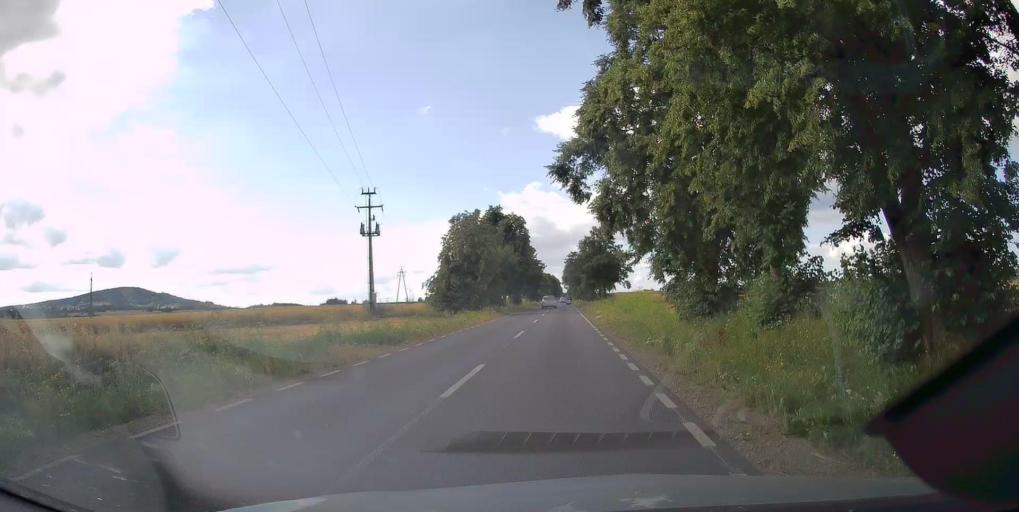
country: PL
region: Swietokrzyskie
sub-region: Powiat kielecki
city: Bodzentyn
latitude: 50.9225
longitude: 20.9878
